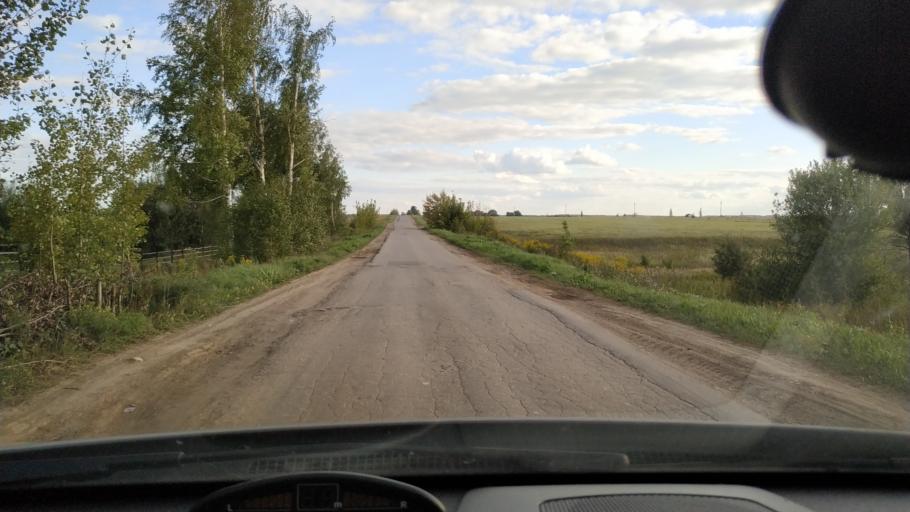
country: RU
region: Rjazan
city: Polyany
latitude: 54.5736
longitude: 39.8615
